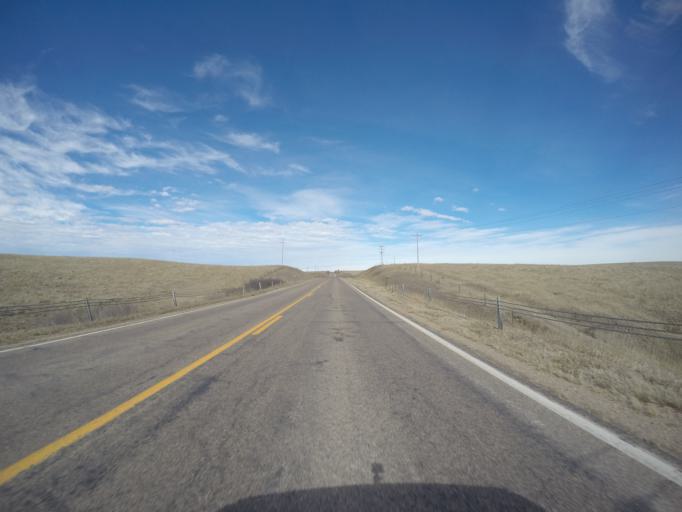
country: US
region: Nebraska
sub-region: Franklin County
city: Franklin
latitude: 40.1451
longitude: -98.9524
